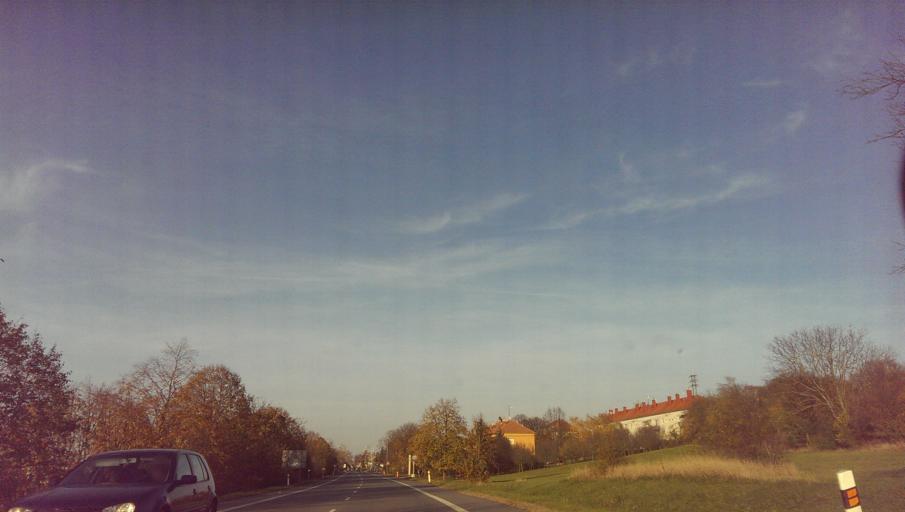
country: CZ
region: Zlin
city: Kunovice
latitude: 49.0302
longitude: 17.4589
